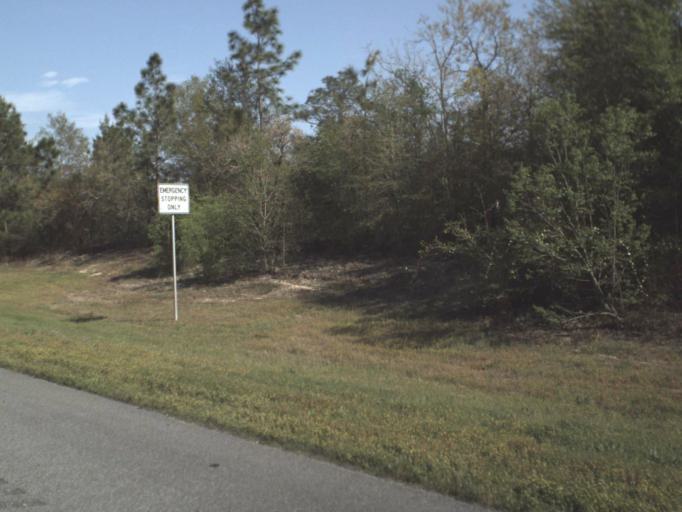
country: US
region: Florida
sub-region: Okaloosa County
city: Crestview
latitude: 30.7265
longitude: -86.5455
